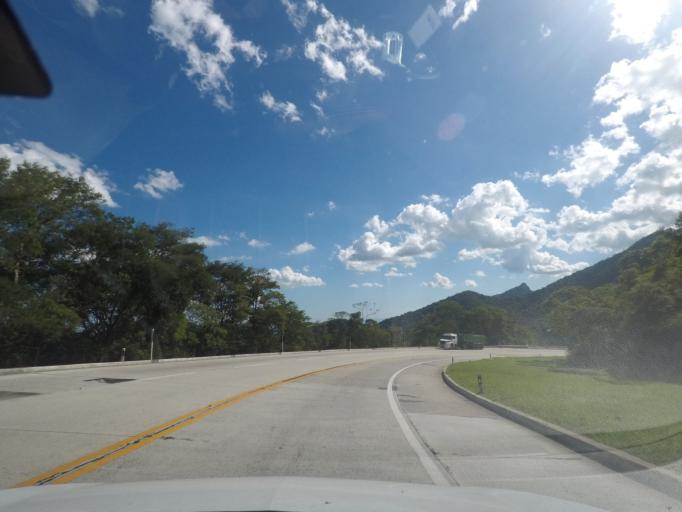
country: BR
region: Rio de Janeiro
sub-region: Guapimirim
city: Guapimirim
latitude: -22.4883
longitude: -42.9976
